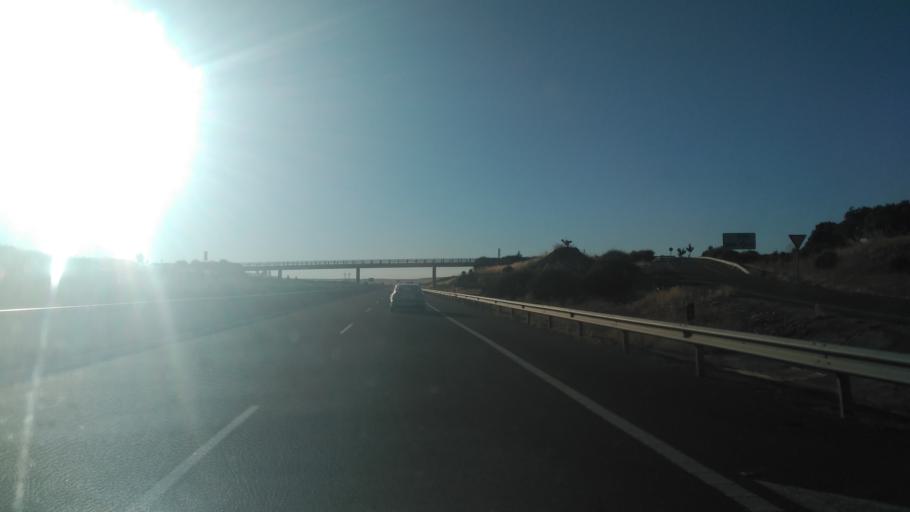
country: ES
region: Castille and Leon
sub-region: Provincia de Salamanca
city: Mozarbez
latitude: 40.8675
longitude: -5.6517
